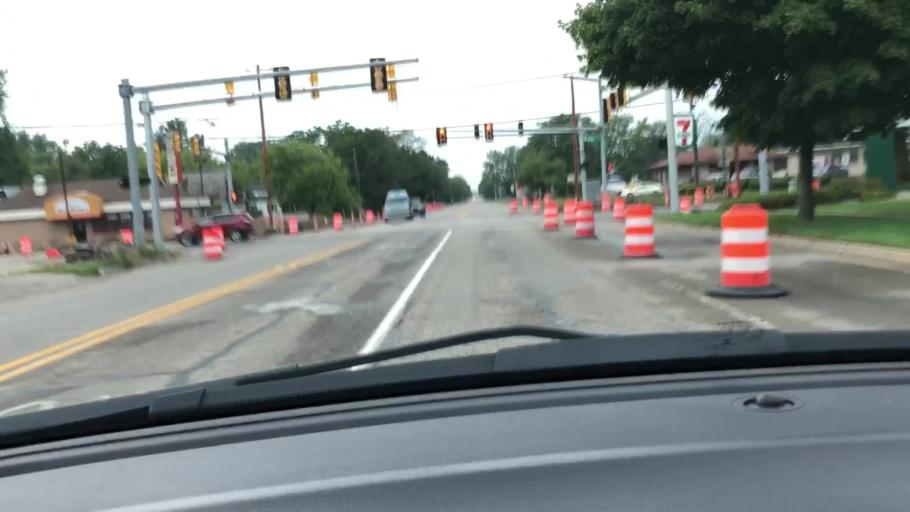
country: US
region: Michigan
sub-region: Midland County
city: Midland
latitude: 43.6050
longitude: -84.1869
